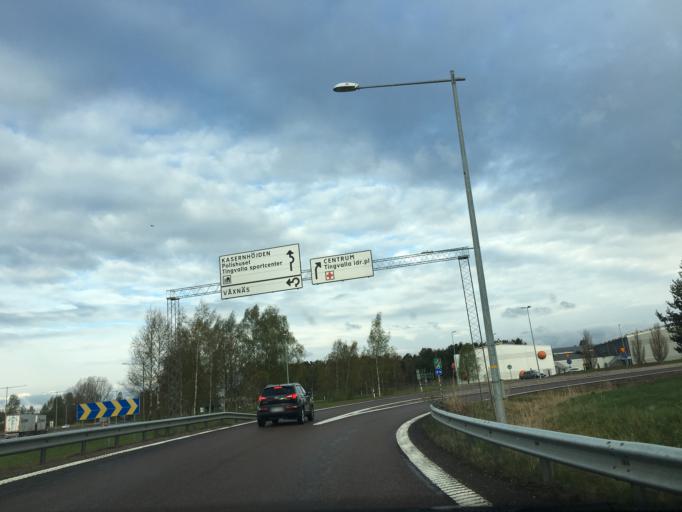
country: SE
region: Vaermland
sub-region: Karlstads Kommun
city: Karlstad
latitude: 59.3851
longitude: 13.4877
